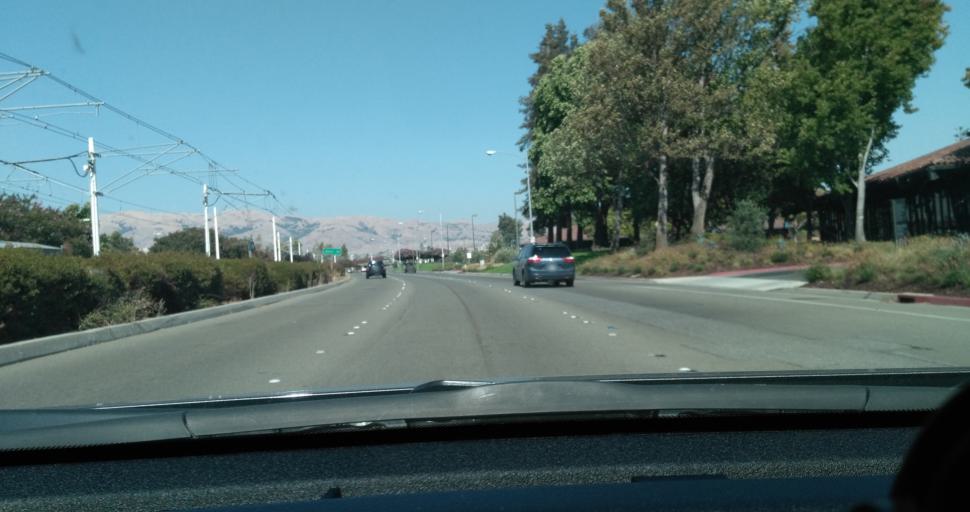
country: US
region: California
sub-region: Santa Clara County
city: Milpitas
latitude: 37.4119
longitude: -121.9188
